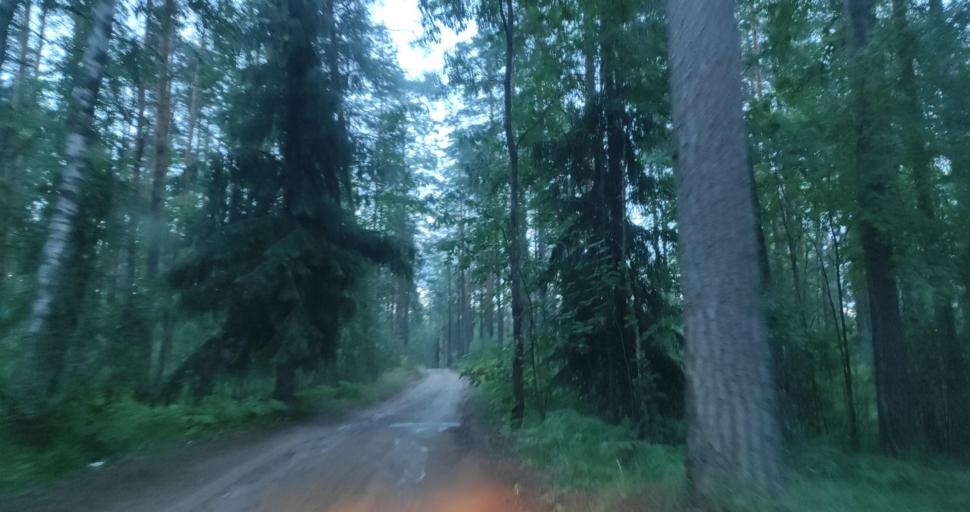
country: RU
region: Leningrad
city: Sapernoye
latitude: 60.6755
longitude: 29.9314
